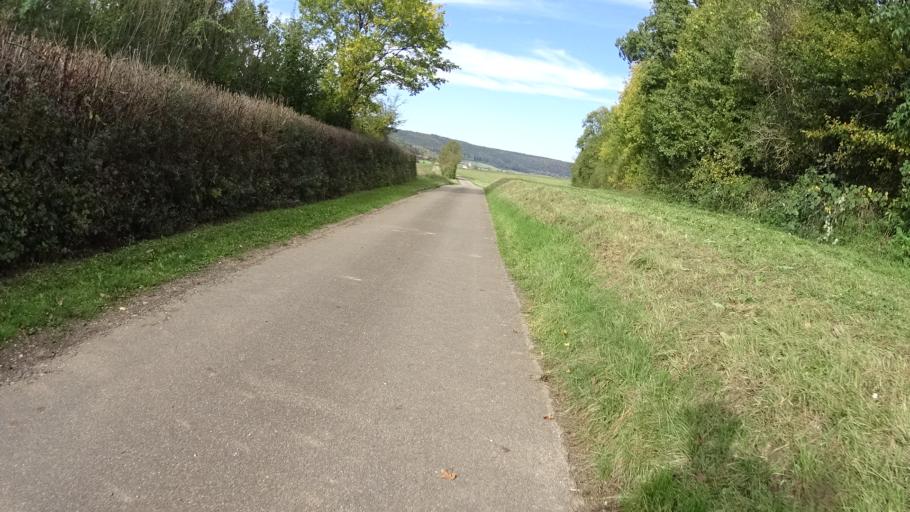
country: DE
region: Bavaria
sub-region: Upper Bavaria
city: Walting
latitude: 48.9153
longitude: 11.3062
